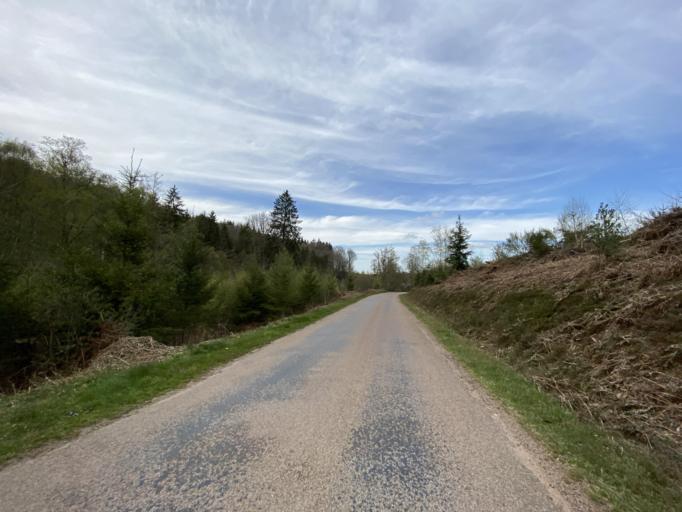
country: FR
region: Bourgogne
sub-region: Departement de la Cote-d'Or
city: Saulieu
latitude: 47.3153
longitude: 4.0938
